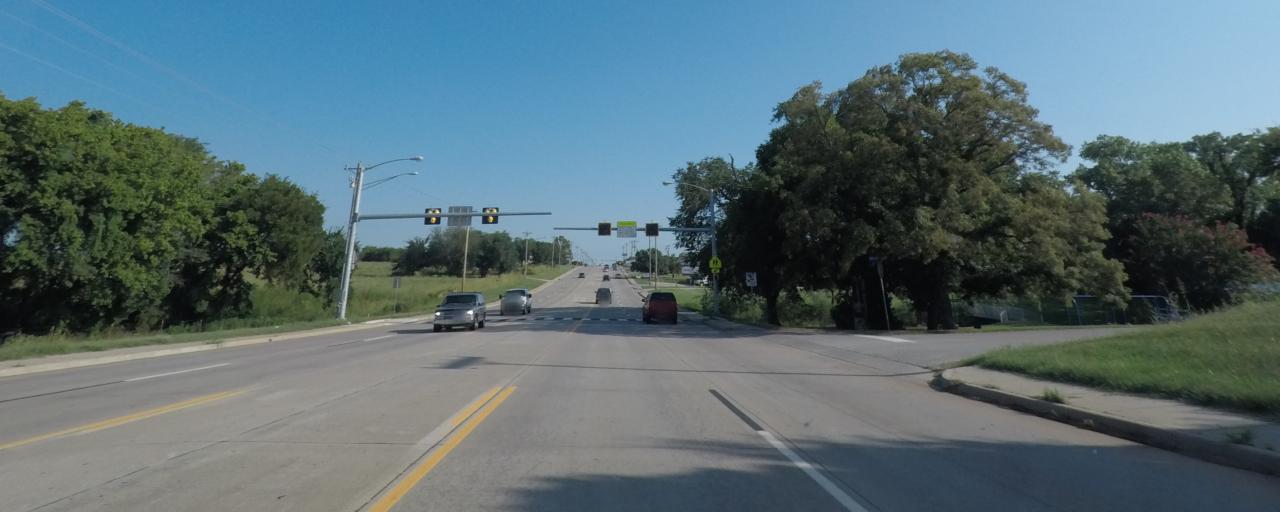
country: US
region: Oklahoma
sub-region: McClain County
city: Newcastle
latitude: 35.2509
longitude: -97.6002
